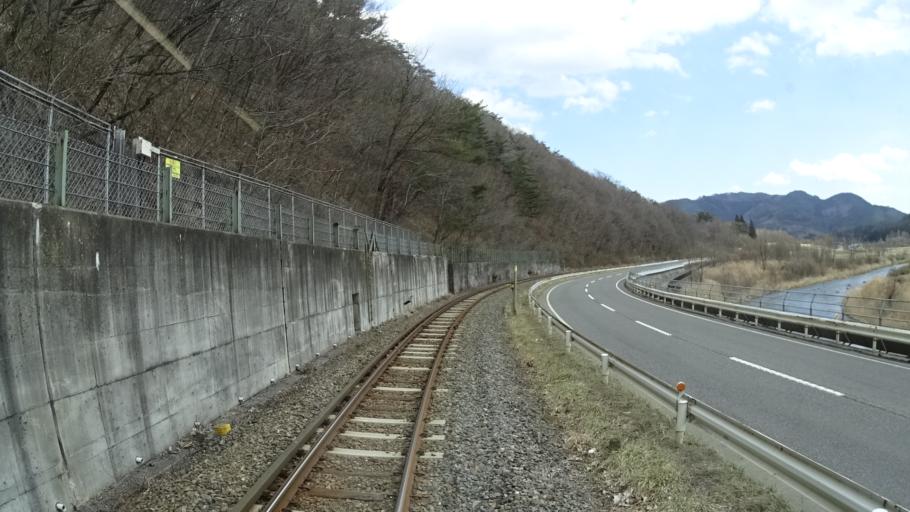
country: JP
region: Iwate
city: Tono
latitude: 39.3040
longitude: 141.3906
